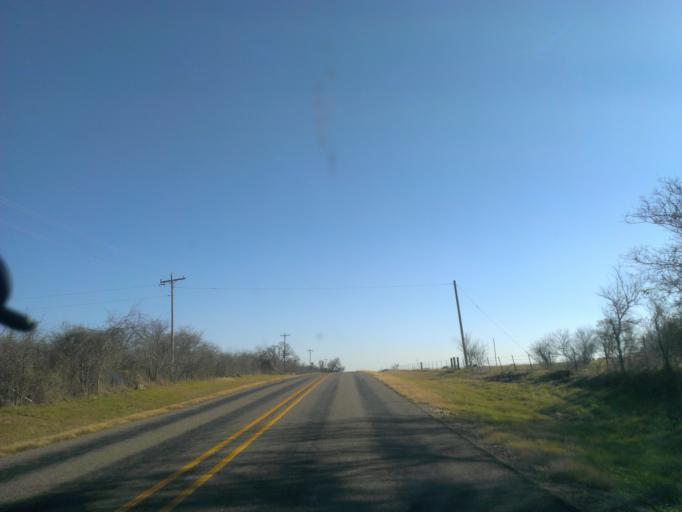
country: US
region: Texas
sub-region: Bastrop County
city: Elgin
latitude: 30.4561
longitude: -97.2683
